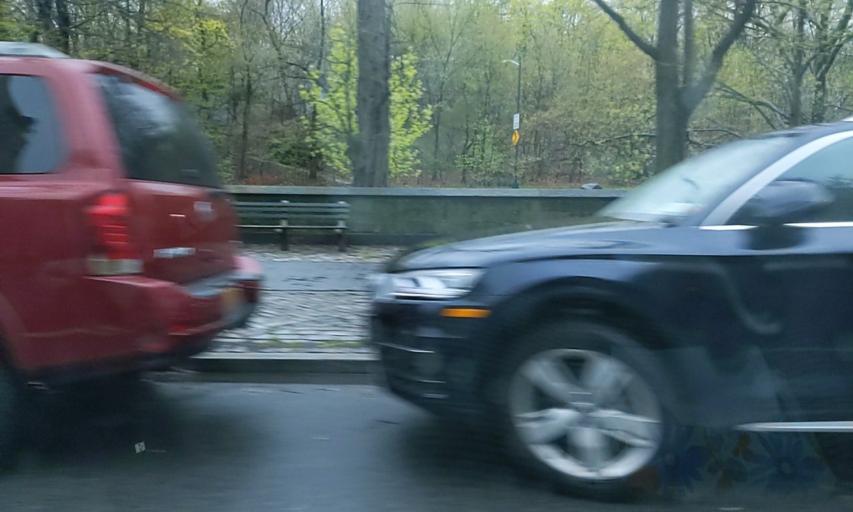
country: US
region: New York
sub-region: New York County
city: Manhattan
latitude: 40.7997
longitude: -73.9561
